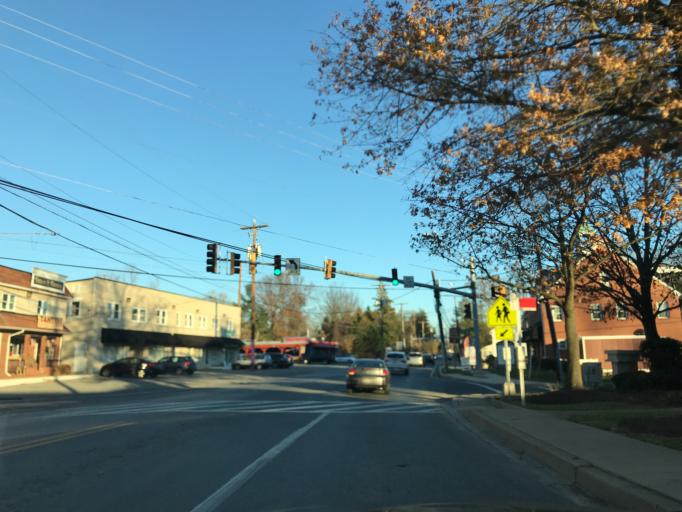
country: US
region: Maryland
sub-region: Montgomery County
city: Ashton-Sandy Spring
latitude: 39.1496
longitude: -77.0271
